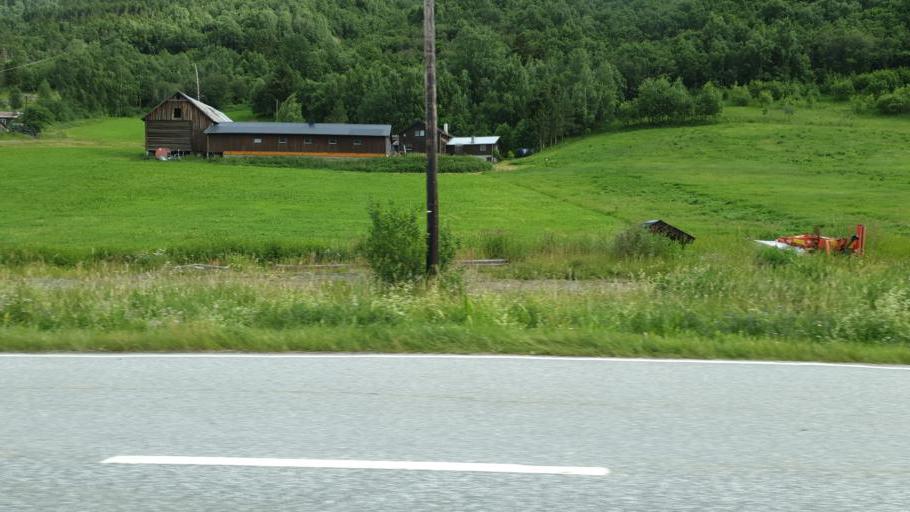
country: NO
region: Oppland
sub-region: Vaga
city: Vagamo
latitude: 61.8569
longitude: 9.0442
